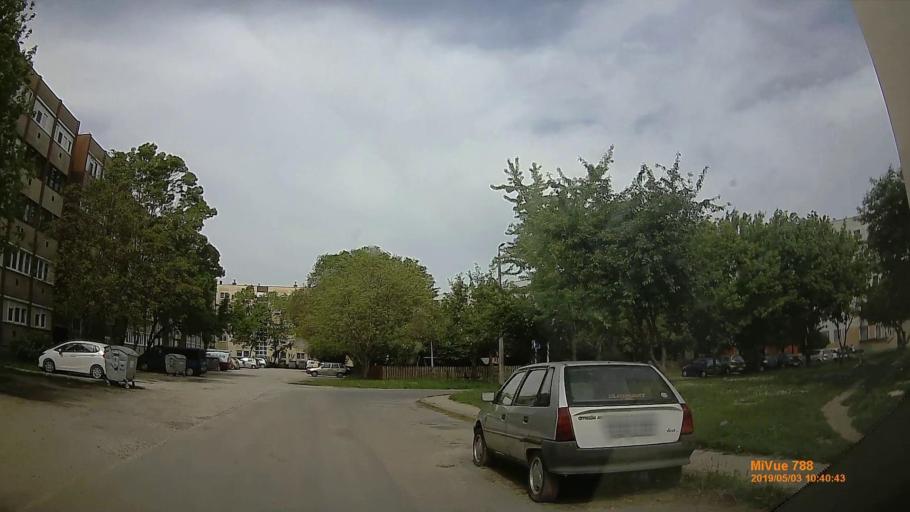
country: HU
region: Jasz-Nagykun-Szolnok
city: Szolnok
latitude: 47.1825
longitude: 20.1942
